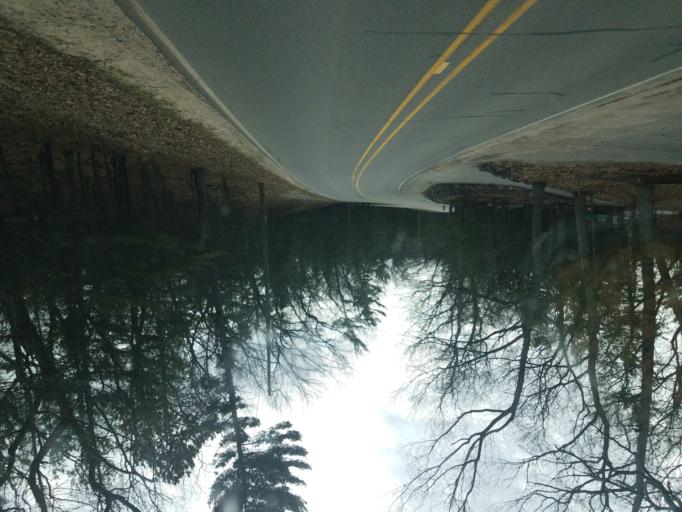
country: US
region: Michigan
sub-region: Oceana County
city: Hart
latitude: 43.7626
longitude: -86.4240
